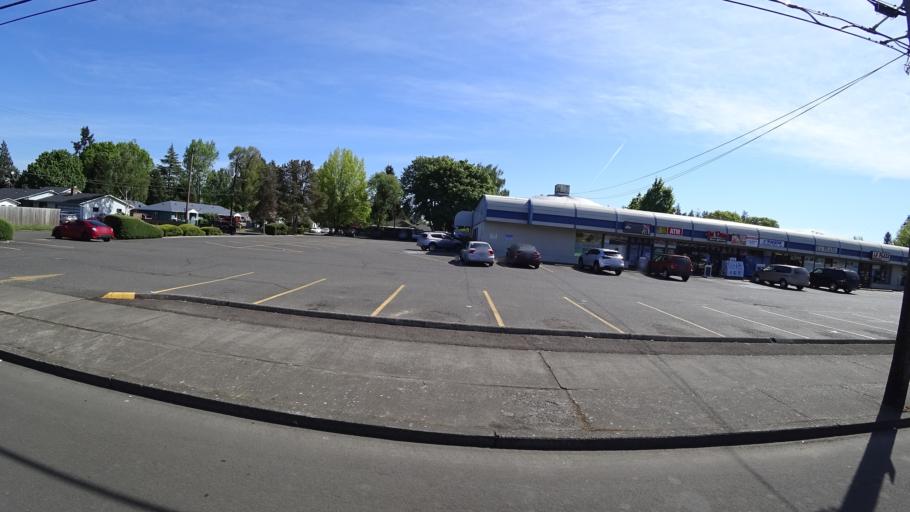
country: US
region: Oregon
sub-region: Washington County
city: Hillsboro
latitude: 45.5174
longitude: -122.9728
